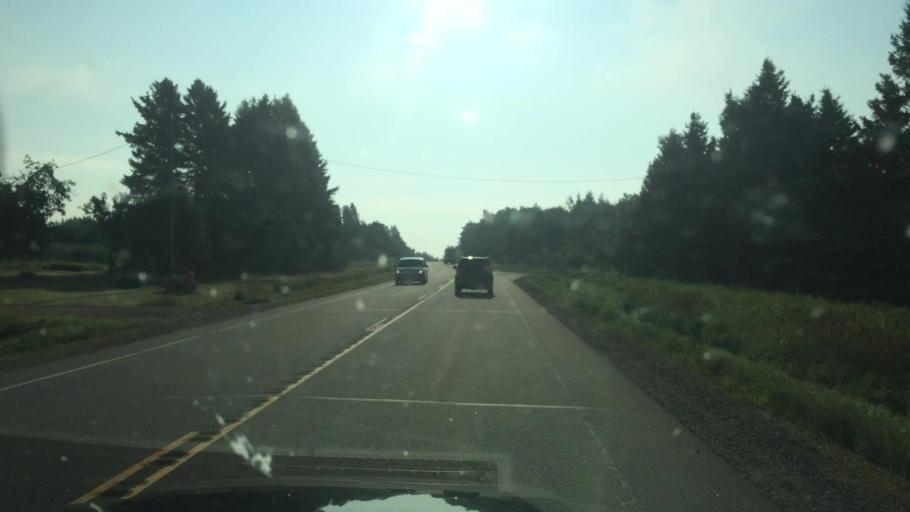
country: US
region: Wisconsin
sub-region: Lincoln County
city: Merrill
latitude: 45.1481
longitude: -89.4273
